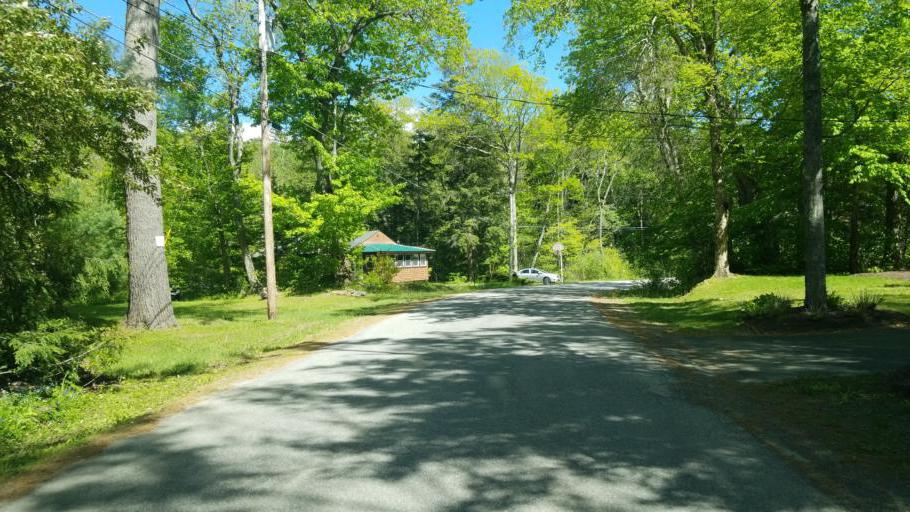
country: US
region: New York
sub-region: Fulton County
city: Gloversville
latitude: 43.1630
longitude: -74.4940
